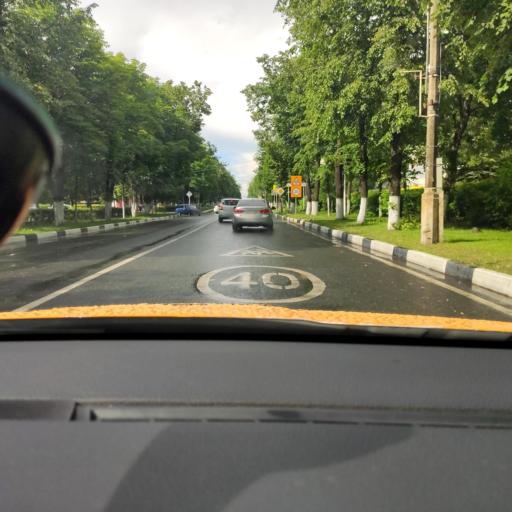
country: RU
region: Moskovskaya
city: Stupino
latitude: 54.8904
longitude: 38.0789
